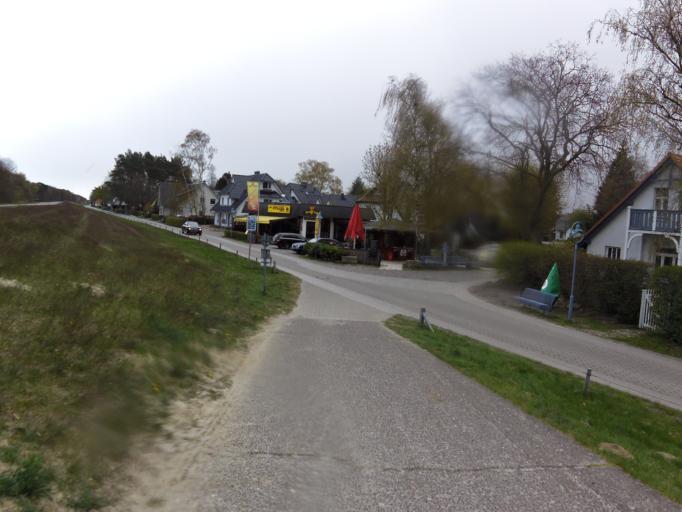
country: DE
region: Mecklenburg-Vorpommern
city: Zingst
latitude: 54.4411
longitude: 12.6926
